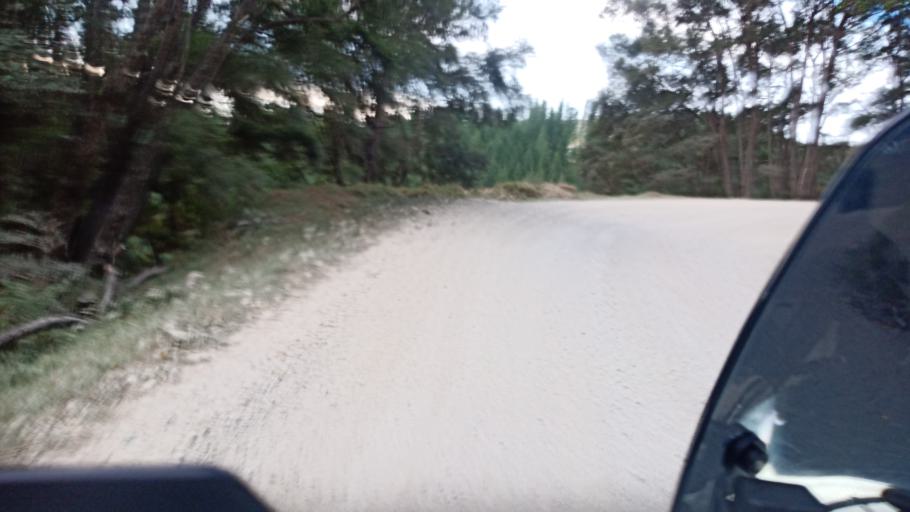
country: NZ
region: Gisborne
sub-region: Gisborne District
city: Gisborne
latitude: -38.4791
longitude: 177.9728
